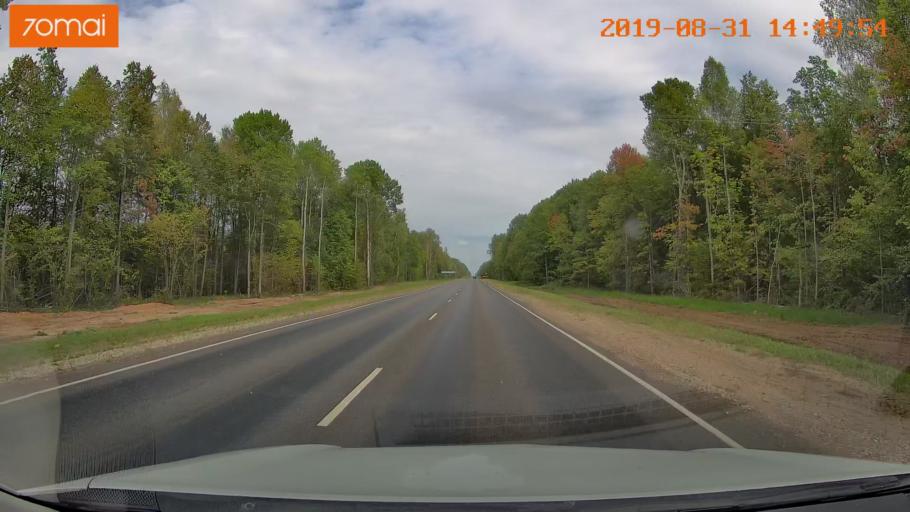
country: RU
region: Kaluga
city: Spas-Demensk
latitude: 54.2575
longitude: 33.7765
